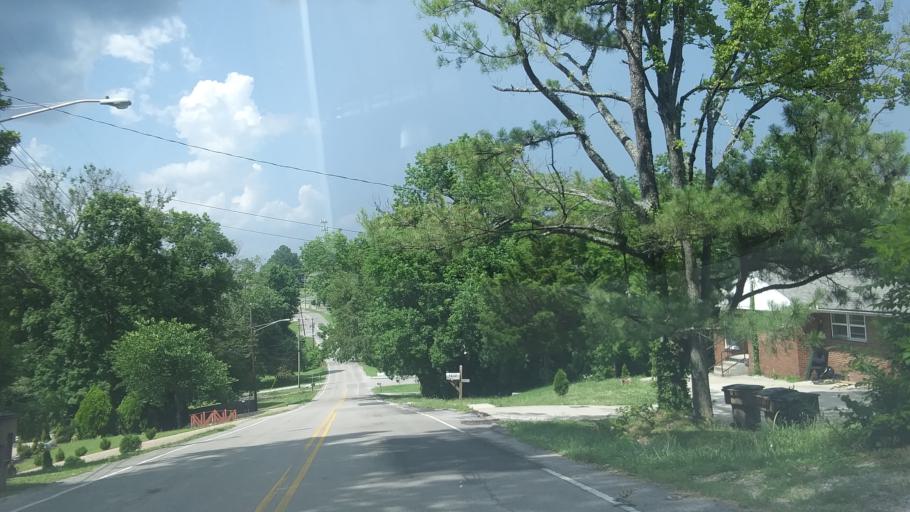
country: US
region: Tennessee
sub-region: Davidson County
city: Oak Hill
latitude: 36.0772
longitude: -86.7150
